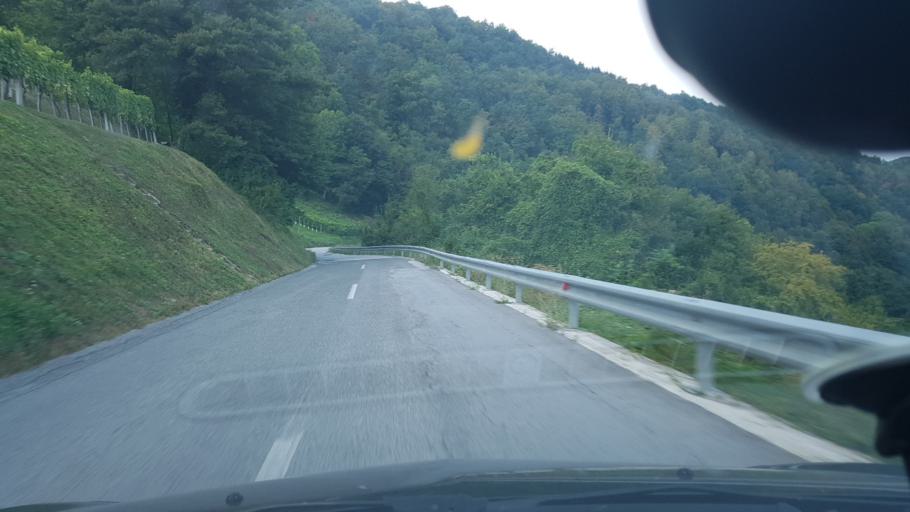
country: SI
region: Kozje
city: Kozje
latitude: 46.0401
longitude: 15.5767
